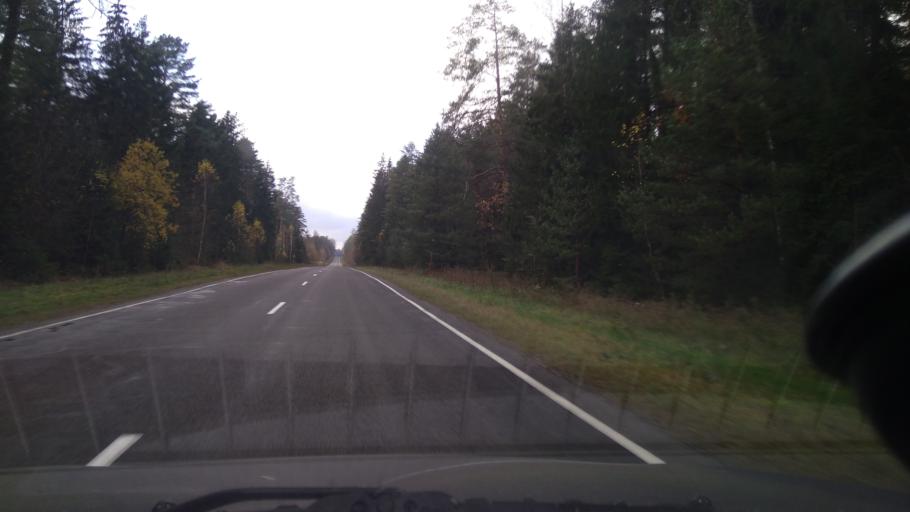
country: BY
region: Minsk
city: Urechcha
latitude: 53.2087
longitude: 27.9527
